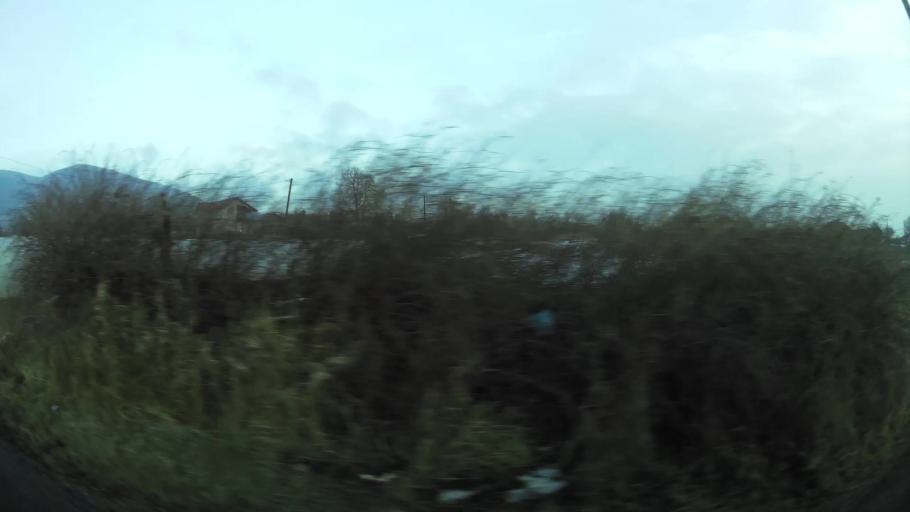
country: MK
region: Aracinovo
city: Arachinovo
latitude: 42.0316
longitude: 21.5461
